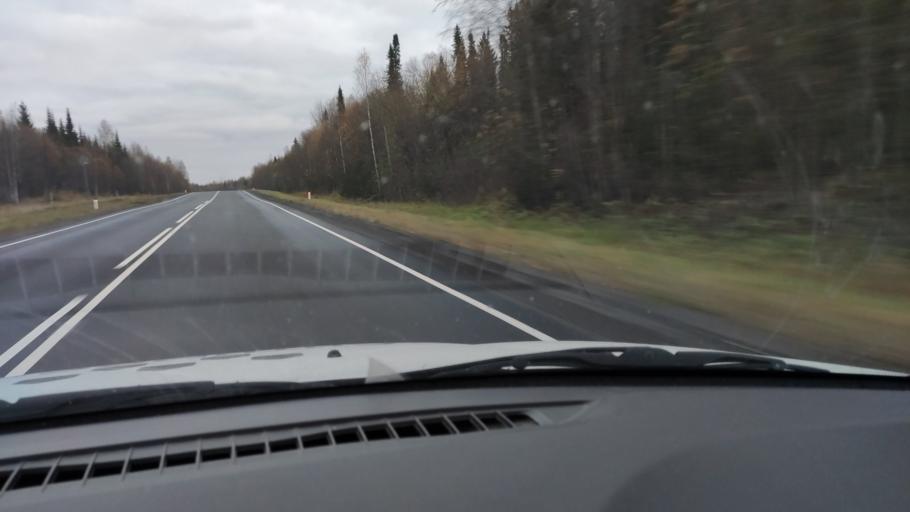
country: RU
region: Kirov
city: Lesnyye Polyany
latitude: 58.8016
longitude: 52.5701
